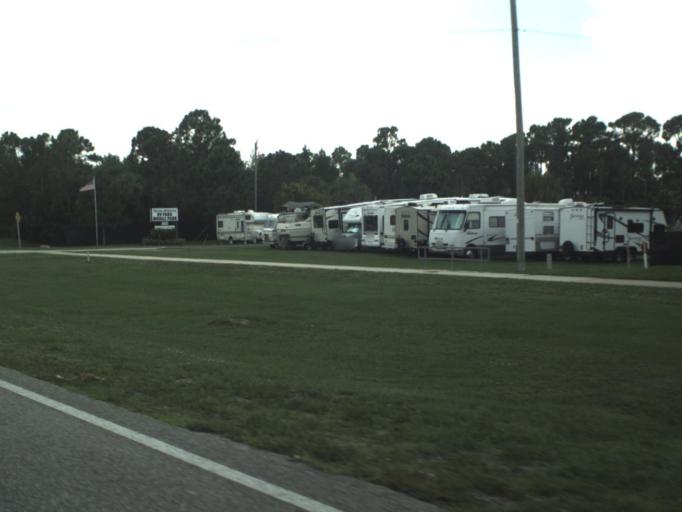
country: US
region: Florida
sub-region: Martin County
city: Port Salerno
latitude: 27.1103
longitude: -80.1710
